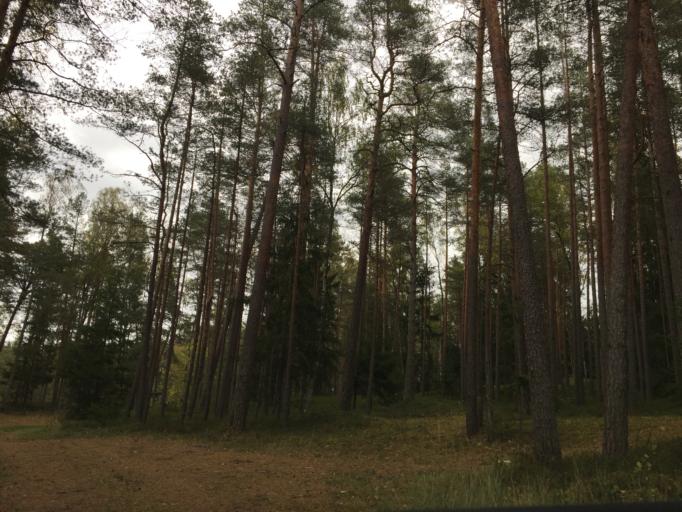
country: LV
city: Tireli
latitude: 56.8764
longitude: 23.5332
